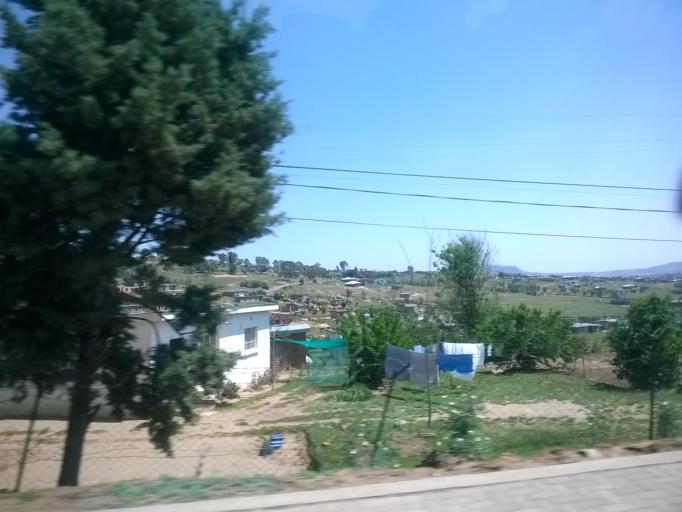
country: LS
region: Berea
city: Teyateyaneng
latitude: -29.1399
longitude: 27.7645
